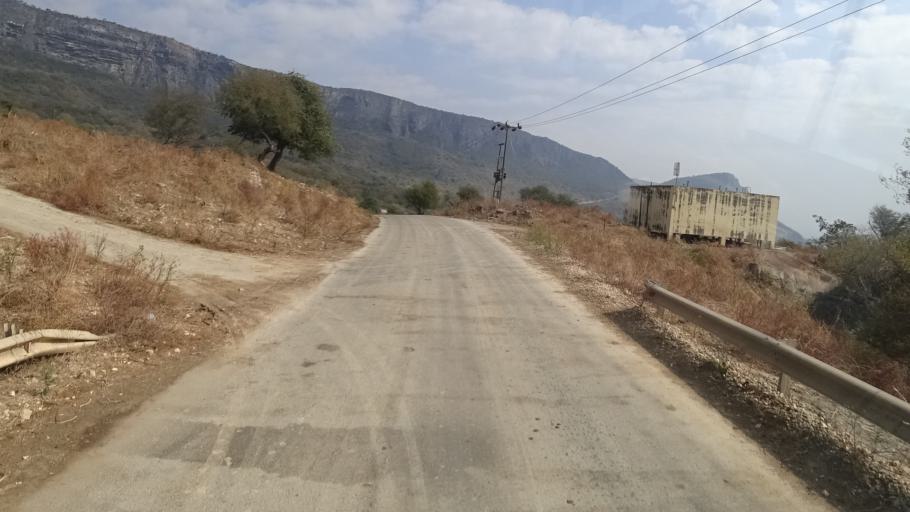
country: YE
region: Al Mahrah
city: Hawf
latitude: 16.7113
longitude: 53.2474
